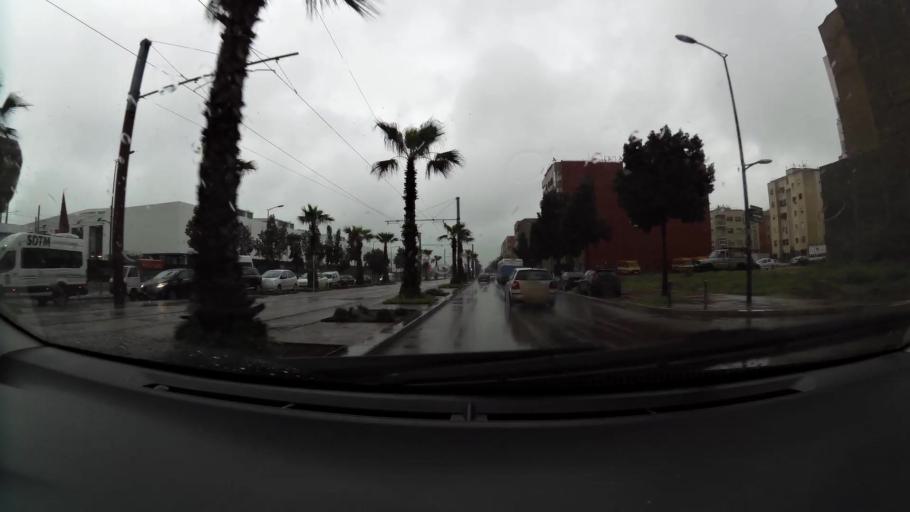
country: MA
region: Grand Casablanca
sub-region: Mediouna
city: Tit Mellil
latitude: 33.5771
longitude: -7.5167
